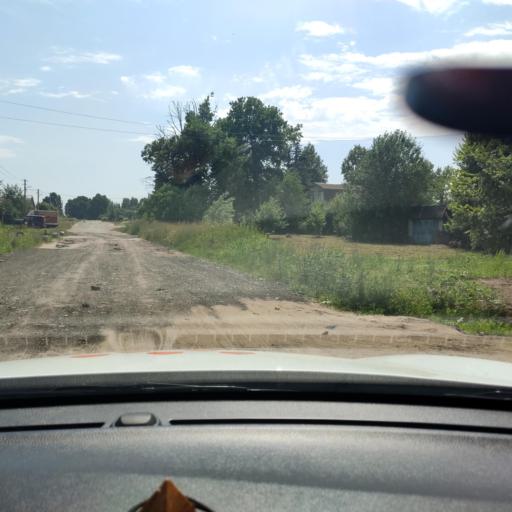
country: RU
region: Tatarstan
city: Osinovo
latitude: 55.9101
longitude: 48.9619
